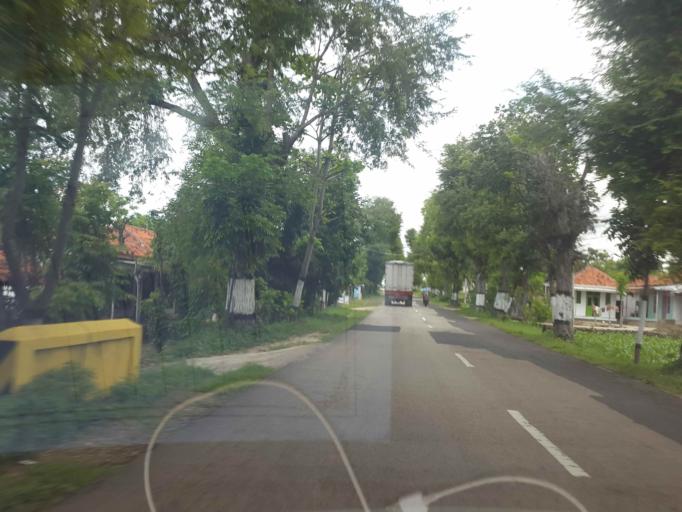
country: ID
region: East Java
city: Pesisir
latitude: -7.1202
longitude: 113.7809
